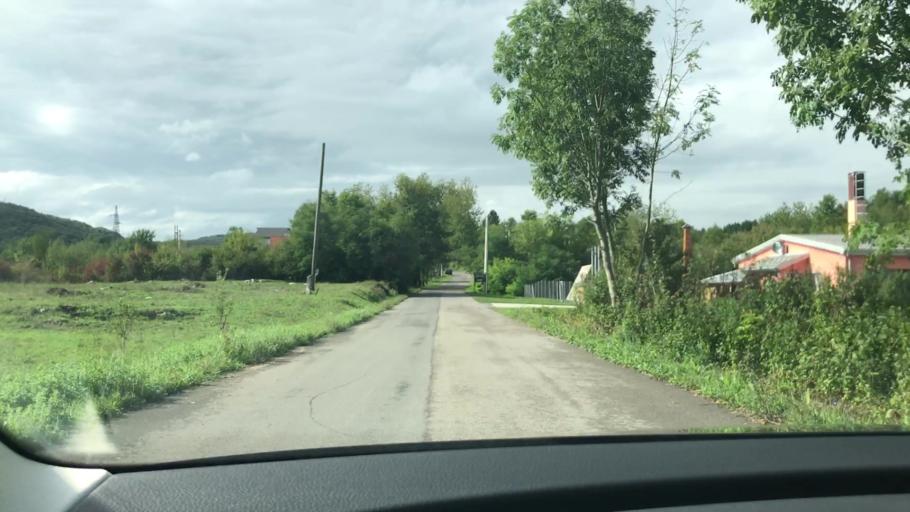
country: BA
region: Federation of Bosnia and Herzegovina
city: Izacic
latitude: 44.8757
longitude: 15.7164
